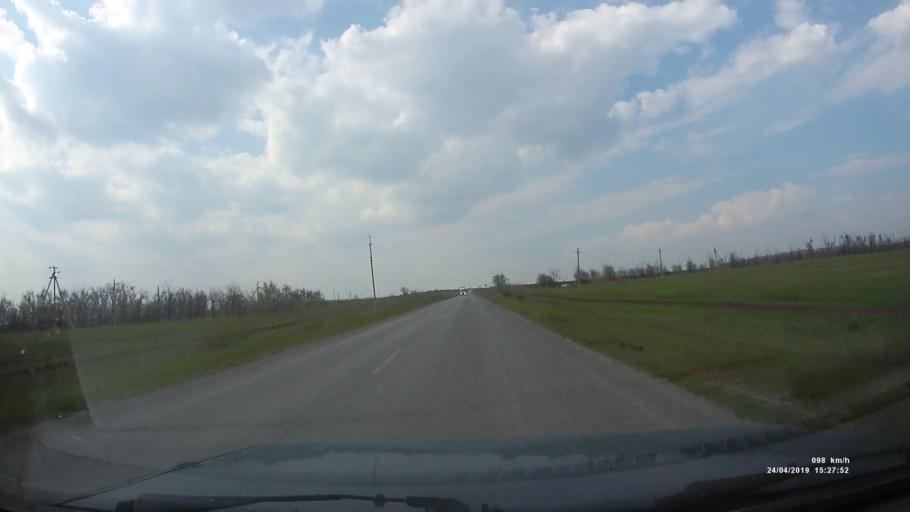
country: RU
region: Rostov
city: Remontnoye
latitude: 46.5708
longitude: 43.0227
